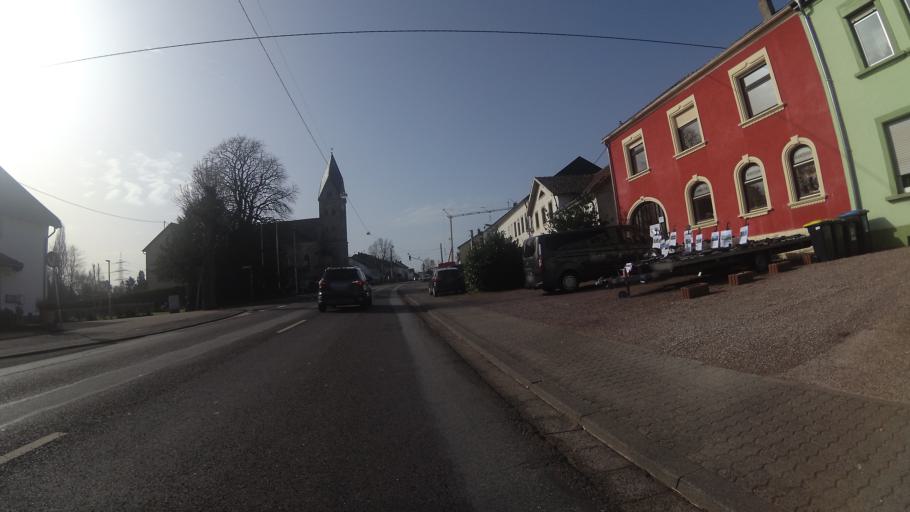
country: DE
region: Saarland
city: Saarlouis
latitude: 49.2868
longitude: 6.7312
